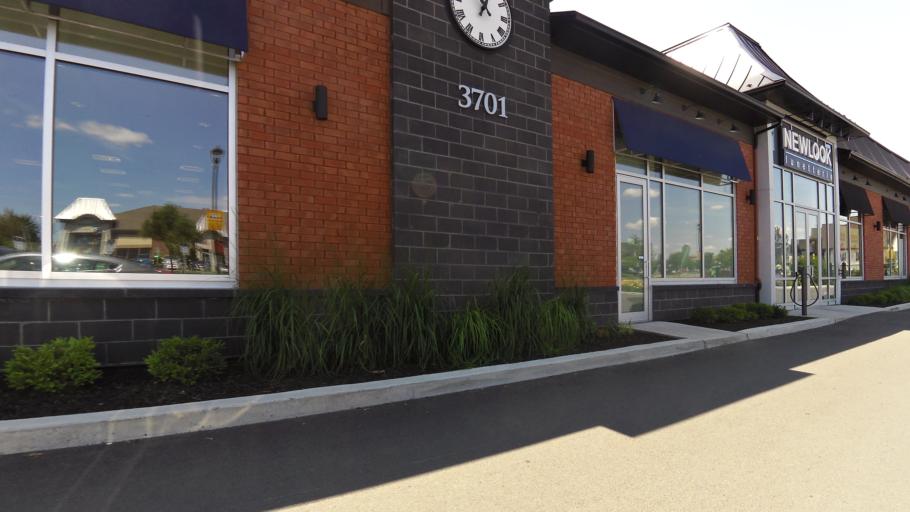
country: CA
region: Quebec
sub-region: Monteregie
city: Carignan
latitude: 45.4274
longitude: -73.3110
